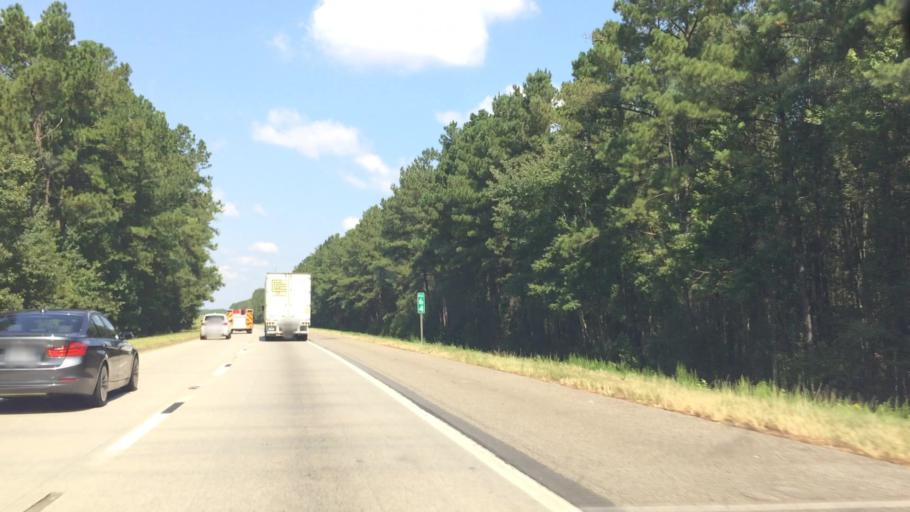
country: US
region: South Carolina
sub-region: Colleton County
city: Walterboro
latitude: 33.0234
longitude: -80.6655
